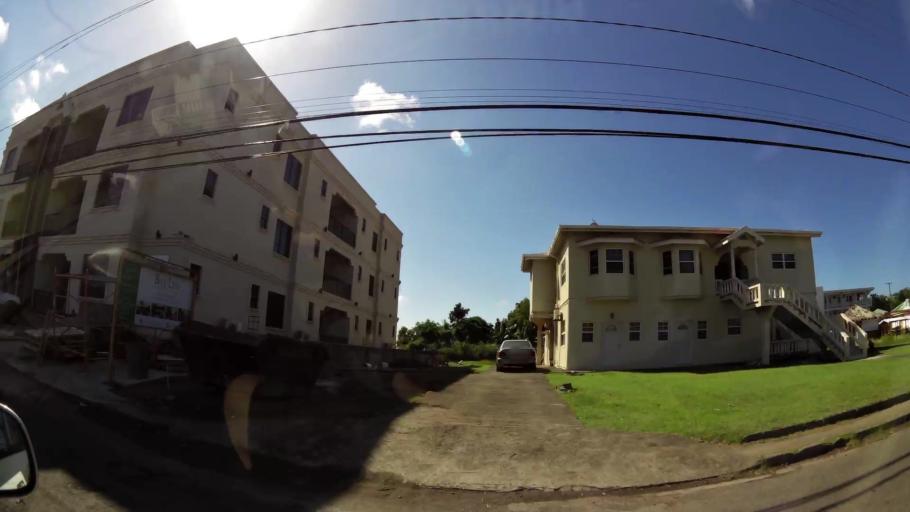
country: GD
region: Saint George
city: Saint George's
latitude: 12.0042
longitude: -61.7704
